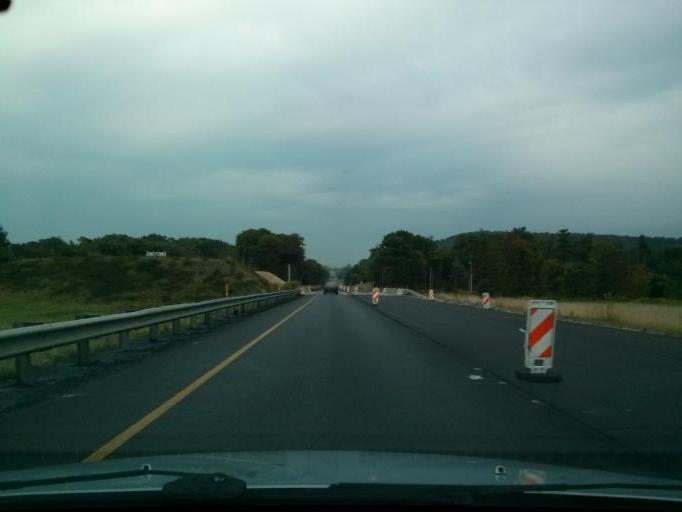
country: US
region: Pennsylvania
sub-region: Jefferson County
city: Reynoldsville
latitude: 41.1521
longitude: -78.9116
